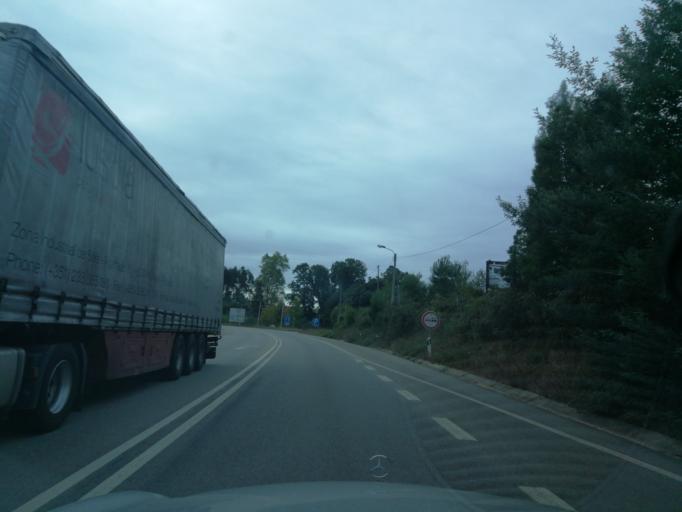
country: PT
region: Aveiro
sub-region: Albergaria-A-Velha
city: Albergaria-a-Velha
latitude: 40.6624
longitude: -8.4753
